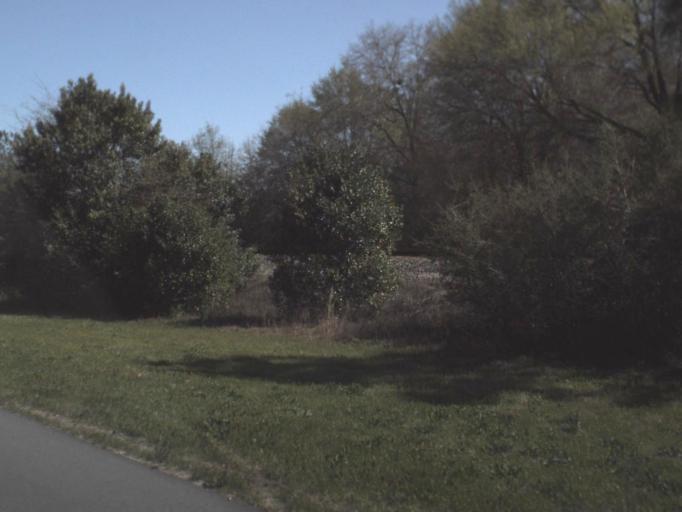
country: US
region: Florida
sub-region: Walton County
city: DeFuniak Springs
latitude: 30.7386
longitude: -86.1740
